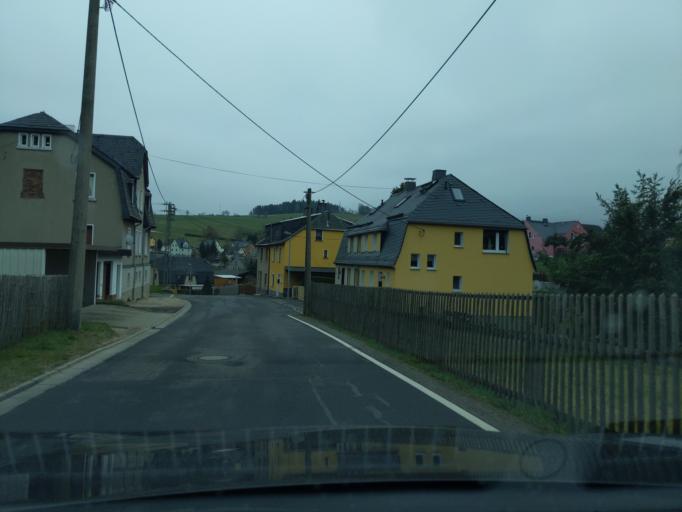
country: DE
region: Saxony
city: Zschorlau
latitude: 50.5726
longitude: 12.6535
